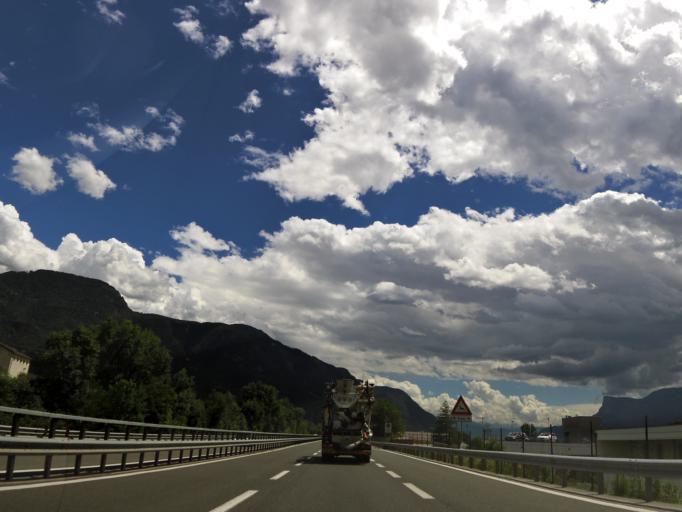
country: IT
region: Trentino-Alto Adige
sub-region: Bolzano
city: Marlengo
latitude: 46.6533
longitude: 11.1501
